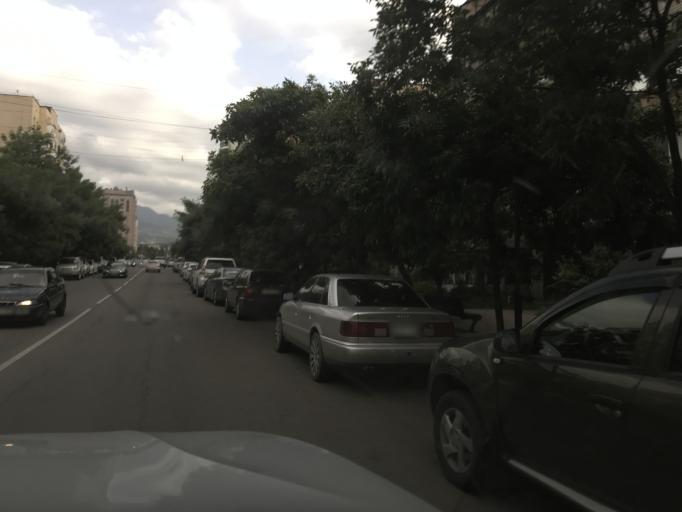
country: KZ
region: Almaty Qalasy
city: Almaty
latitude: 43.2304
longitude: 76.9537
